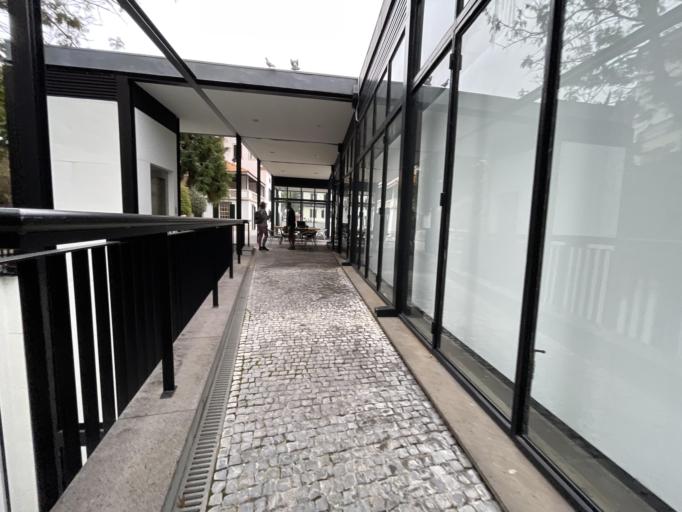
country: PT
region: Madeira
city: Ponta do Sol
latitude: 32.6807
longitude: -17.1048
